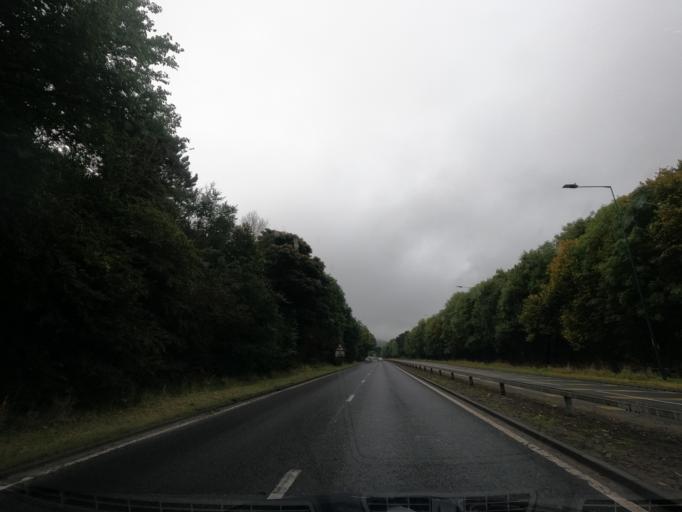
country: GB
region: England
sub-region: Redcar and Cleveland
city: Redcar
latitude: 54.5819
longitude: -1.0895
